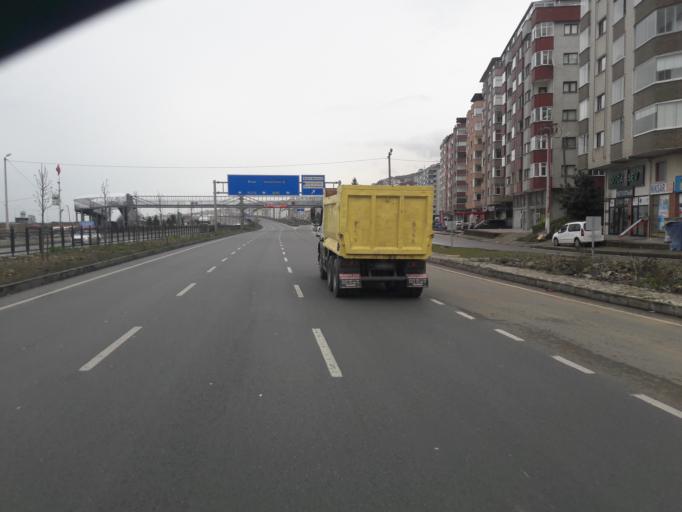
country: TR
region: Trabzon
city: Trabzon
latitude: 40.9944
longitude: 39.6569
